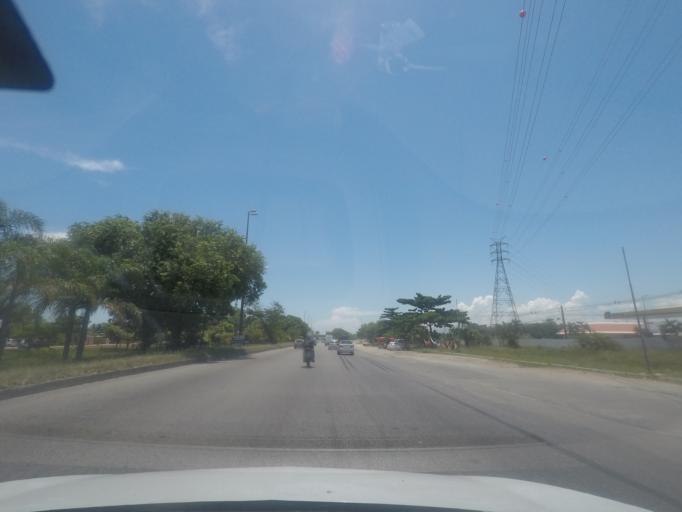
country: BR
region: Rio de Janeiro
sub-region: Itaguai
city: Itaguai
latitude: -22.8945
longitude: -43.6784
